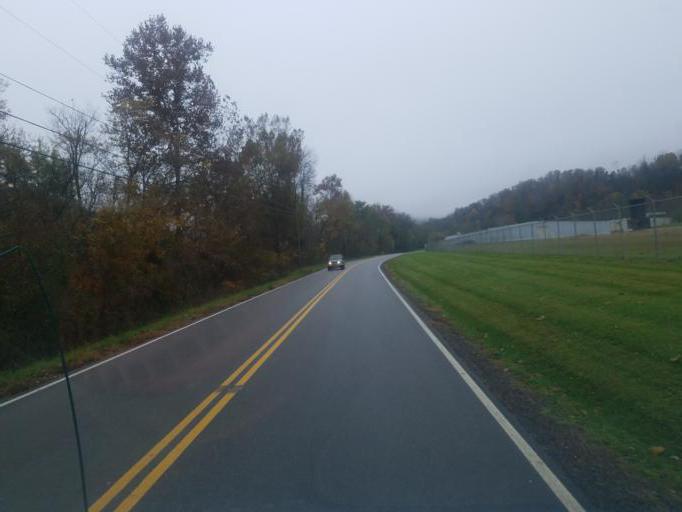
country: US
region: Ohio
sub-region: Morgan County
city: McConnelsville
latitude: 39.6287
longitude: -81.8377
